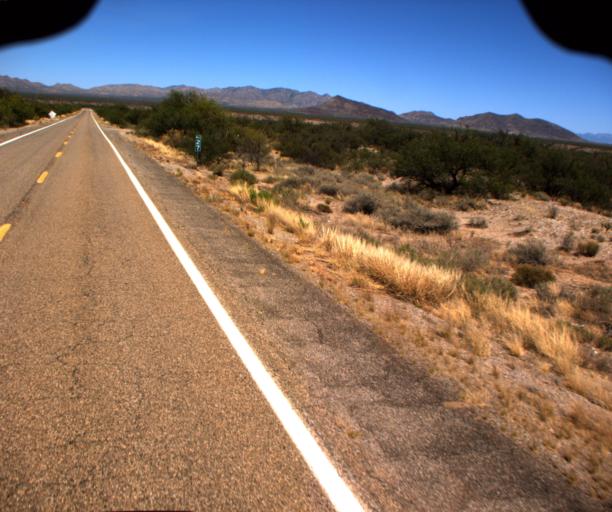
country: US
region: Arizona
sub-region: Pima County
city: Three Points
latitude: 31.8356
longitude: -111.4107
